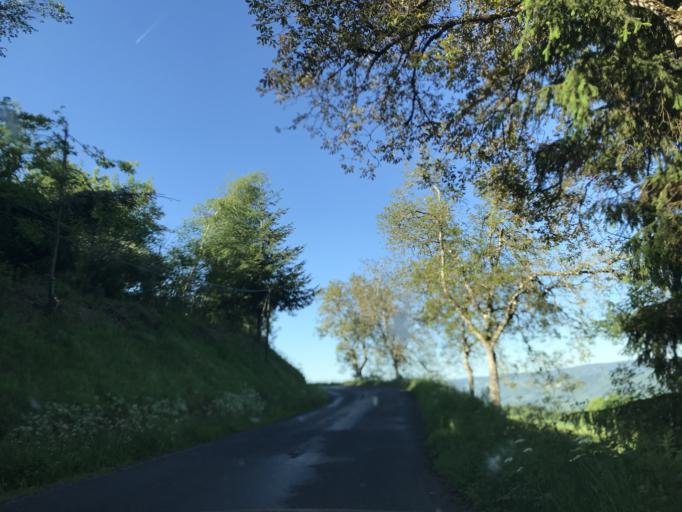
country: FR
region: Auvergne
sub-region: Departement du Puy-de-Dome
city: Job
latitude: 45.6763
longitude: 3.7002
